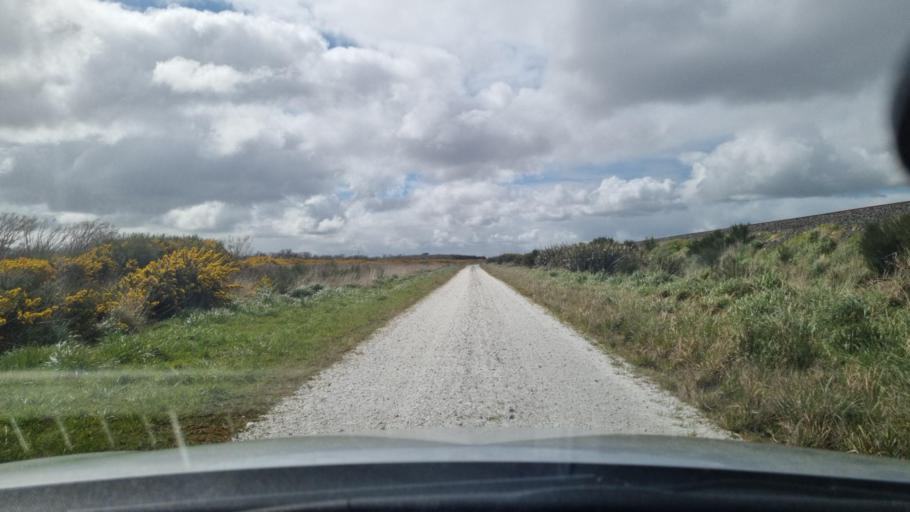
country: NZ
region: Southland
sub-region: Invercargill City
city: Bluff
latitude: -46.5321
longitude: 168.3050
